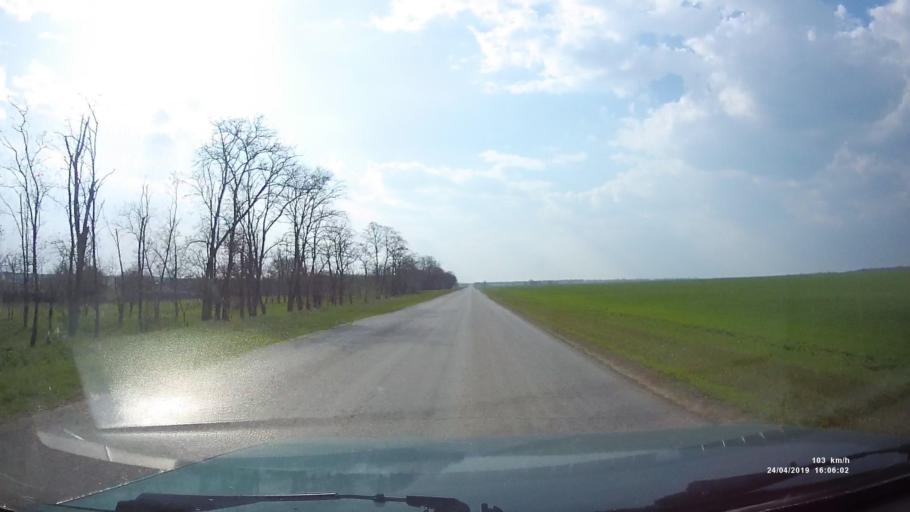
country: RU
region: Rostov
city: Sovetskoye
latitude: 46.6842
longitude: 42.3576
